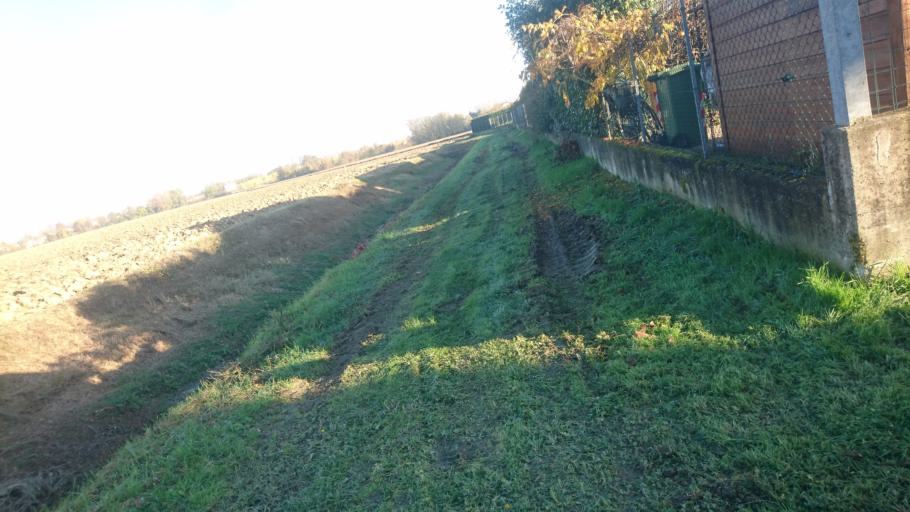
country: IT
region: Veneto
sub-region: Provincia di Padova
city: Villaguattera
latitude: 45.4457
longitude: 11.8210
